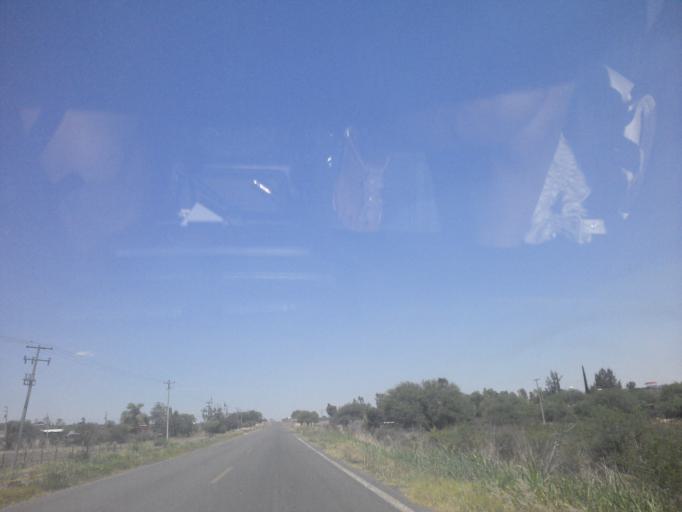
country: MX
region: Guanajuato
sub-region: San Francisco del Rincon
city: San Ignacio de Hidalgo
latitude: 20.8919
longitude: -101.9512
